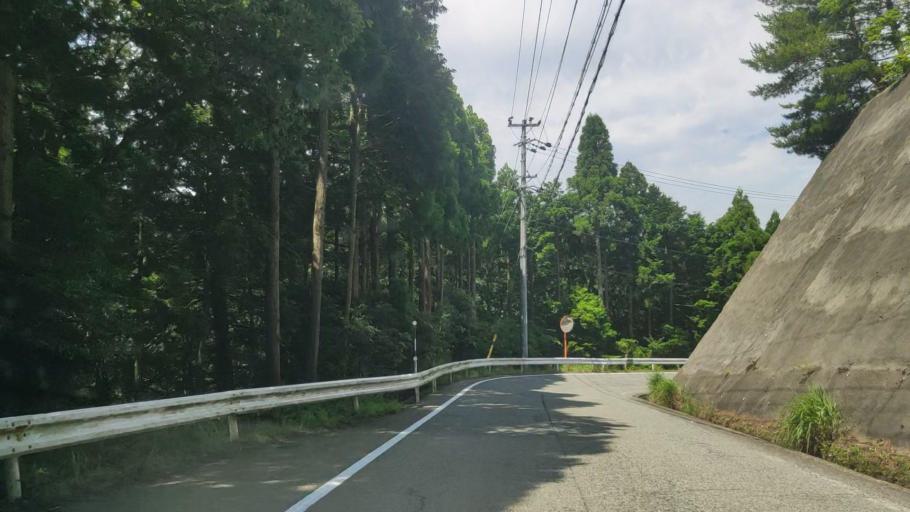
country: JP
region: Hyogo
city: Toyooka
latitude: 35.6388
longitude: 134.7690
